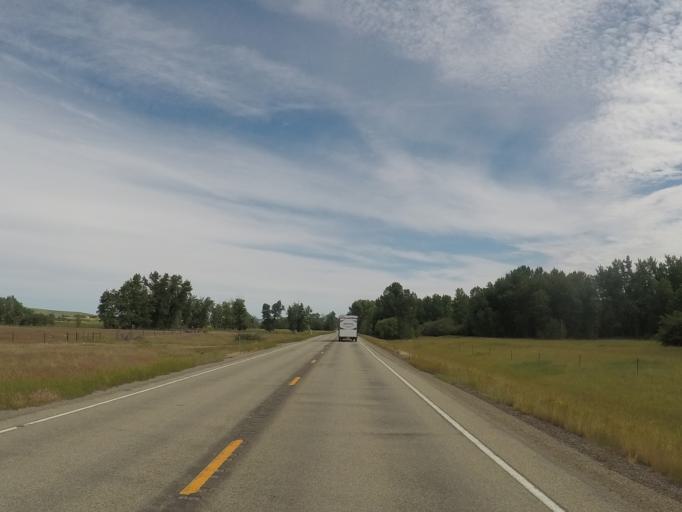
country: US
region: Montana
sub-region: Carbon County
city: Red Lodge
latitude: 45.3212
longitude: -109.1911
